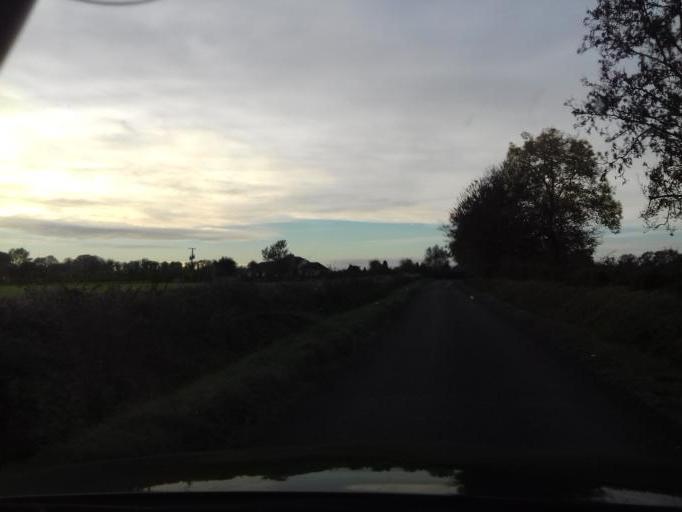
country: IE
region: Leinster
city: Hartstown
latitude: 53.3832
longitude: -6.4486
